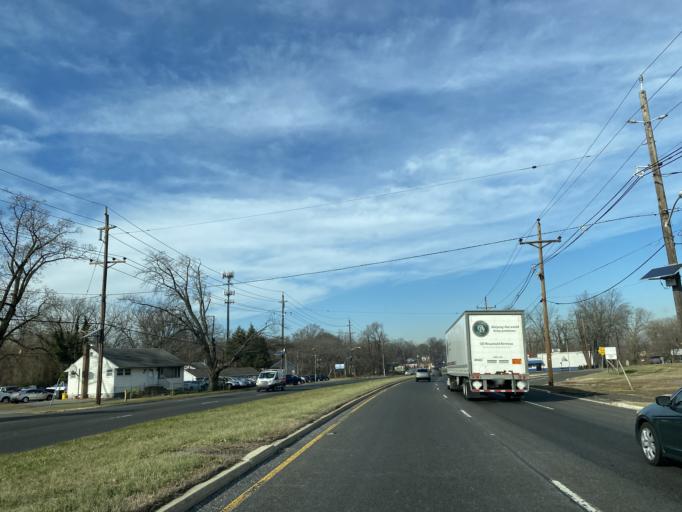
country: US
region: New Jersey
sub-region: Burlington County
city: Maple Shade
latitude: 39.9651
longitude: -75.0000
